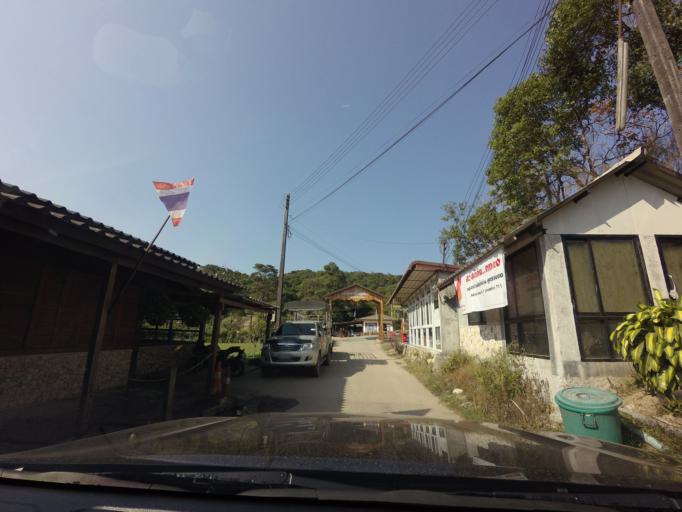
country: TH
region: Kanchanaburi
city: Thong Pha Phum
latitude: 14.6785
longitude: 98.3680
